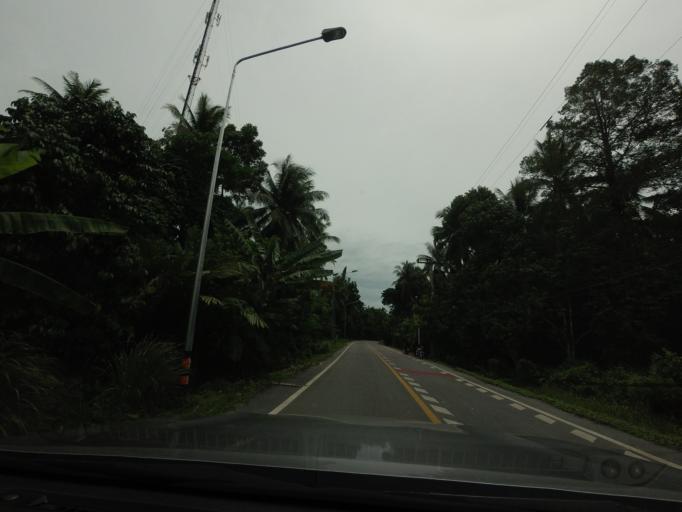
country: TH
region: Pattani
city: Kapho
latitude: 6.5966
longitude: 101.5304
